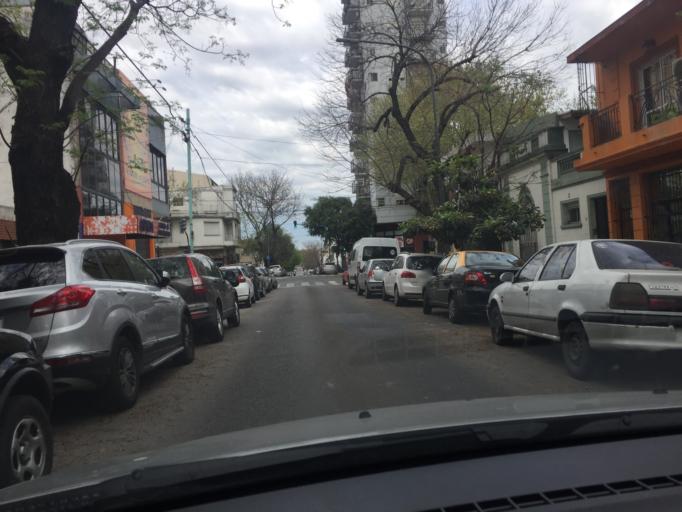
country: AR
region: Buenos Aires
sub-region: Partido de General San Martin
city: General San Martin
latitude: -34.5691
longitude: -58.4915
